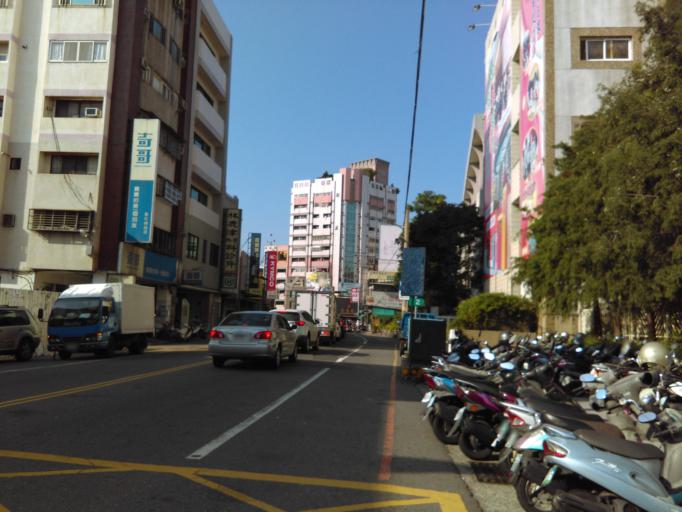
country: TW
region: Taiwan
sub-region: Changhua
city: Chang-hua
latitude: 24.0842
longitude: 120.5423
